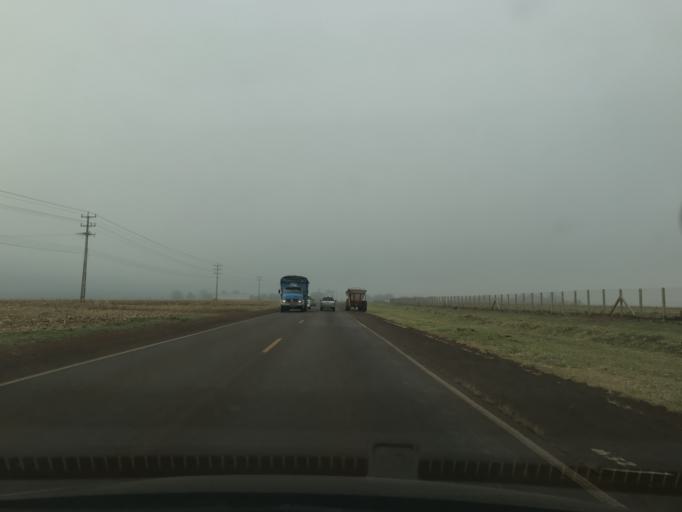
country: BR
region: Parana
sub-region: Toledo
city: Toledo
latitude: -24.6918
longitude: -53.6962
